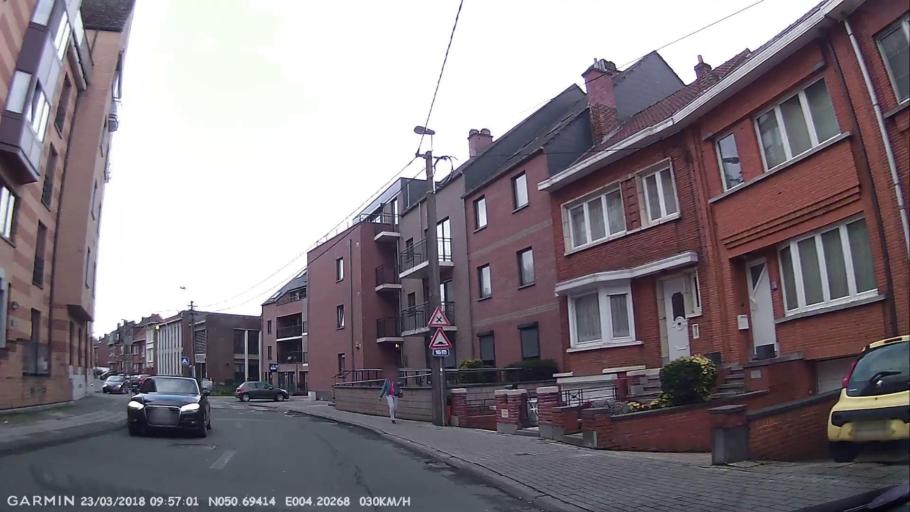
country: BE
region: Wallonia
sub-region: Province du Brabant Wallon
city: Tubize
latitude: 50.6941
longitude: 4.2026
